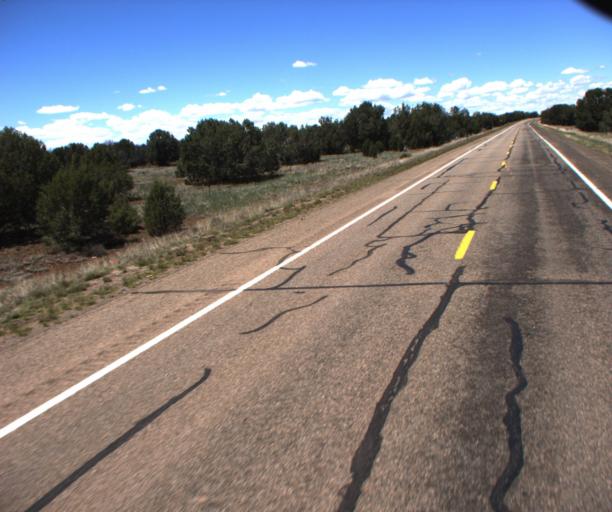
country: US
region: Arizona
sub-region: Yavapai County
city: Paulden
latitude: 35.1585
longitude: -112.4547
